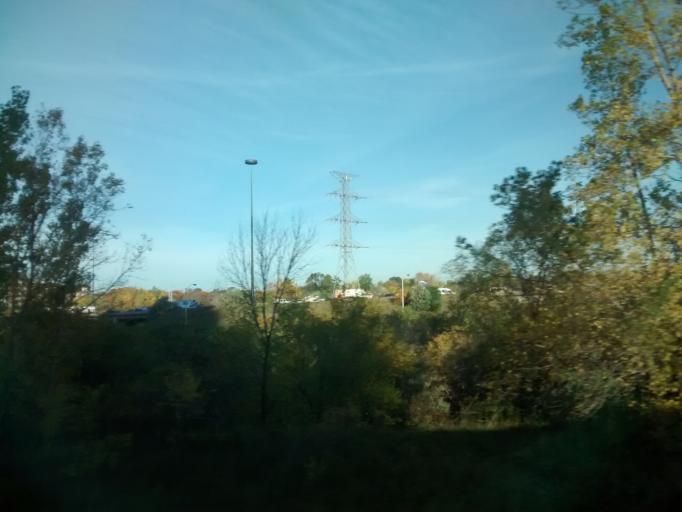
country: CA
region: Ontario
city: Etobicoke
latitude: 43.6248
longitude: -79.4859
